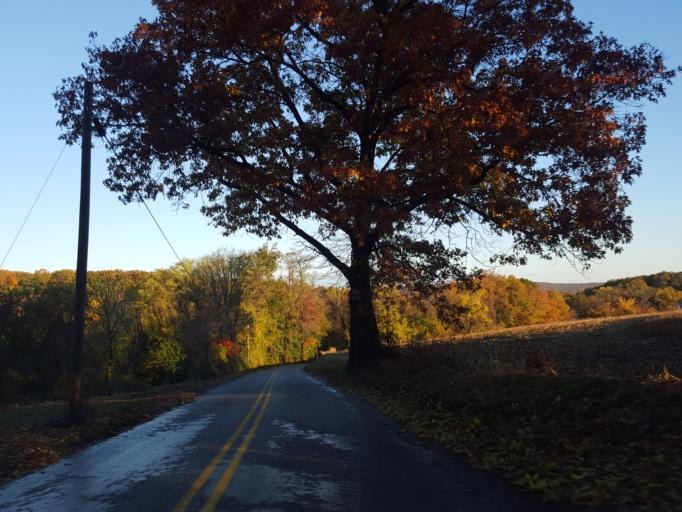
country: US
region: Pennsylvania
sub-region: York County
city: Stonybrook
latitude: 39.9675
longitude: -76.6272
